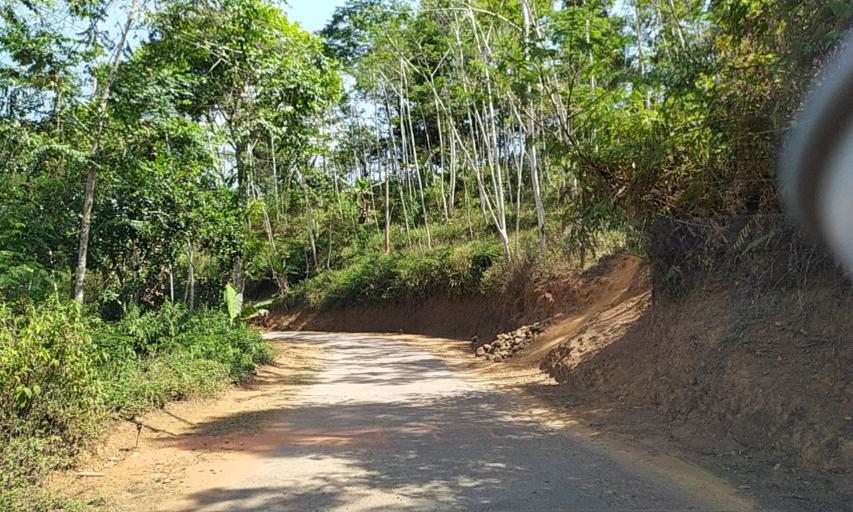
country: ID
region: Central Java
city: Timbang Satu
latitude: -7.2132
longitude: 108.6767
